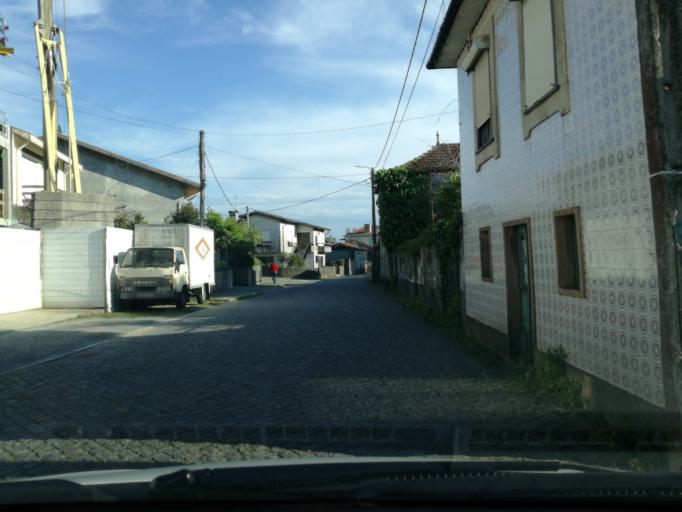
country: PT
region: Porto
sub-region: Maia
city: Gemunde
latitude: 41.2519
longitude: -8.6481
